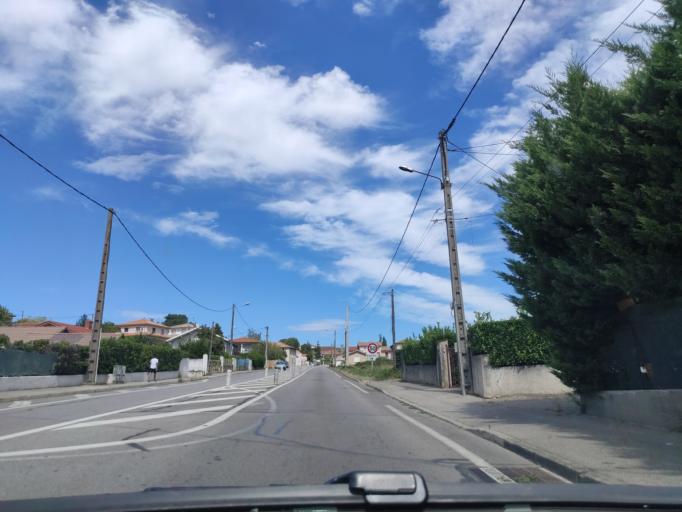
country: FR
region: Rhone-Alpes
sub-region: Departement de l'Isere
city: Le Peage-de-Roussillon
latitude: 45.3809
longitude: 4.7979
